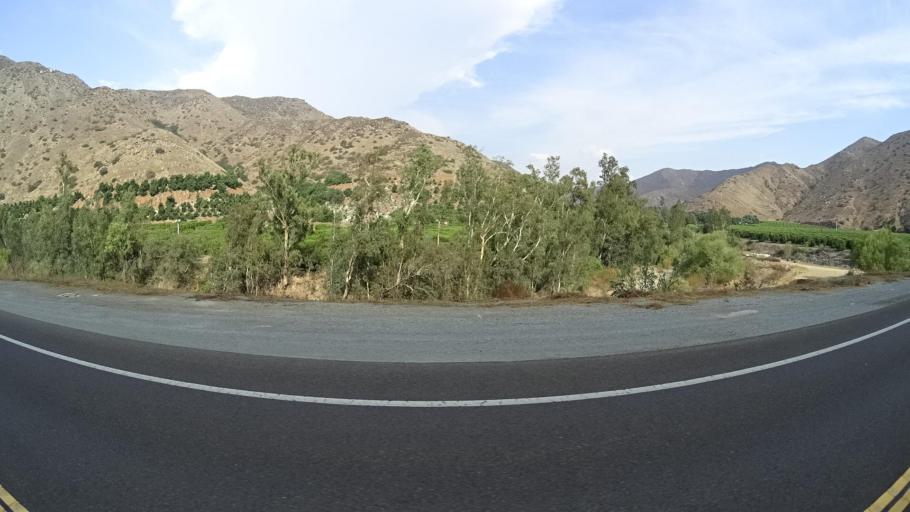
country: US
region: California
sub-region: San Diego County
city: San Pasqual
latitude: 33.0898
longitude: -116.9379
